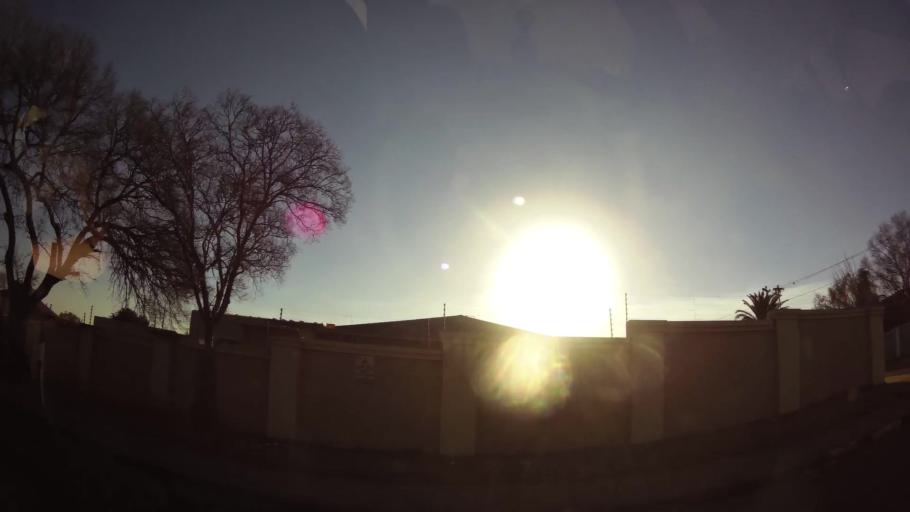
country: ZA
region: Gauteng
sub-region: City of Johannesburg Metropolitan Municipality
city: Roodepoort
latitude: -26.1762
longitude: 27.9383
